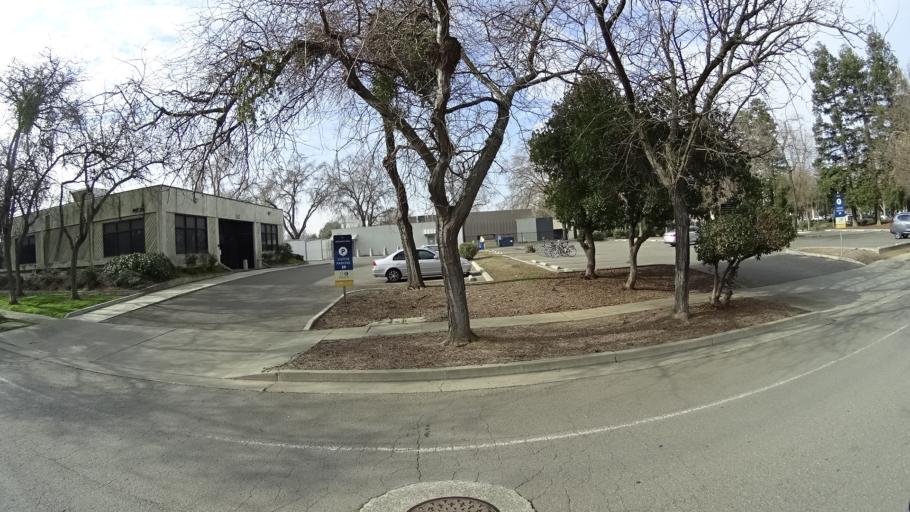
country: US
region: California
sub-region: Yolo County
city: Davis
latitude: 38.5378
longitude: -121.7324
